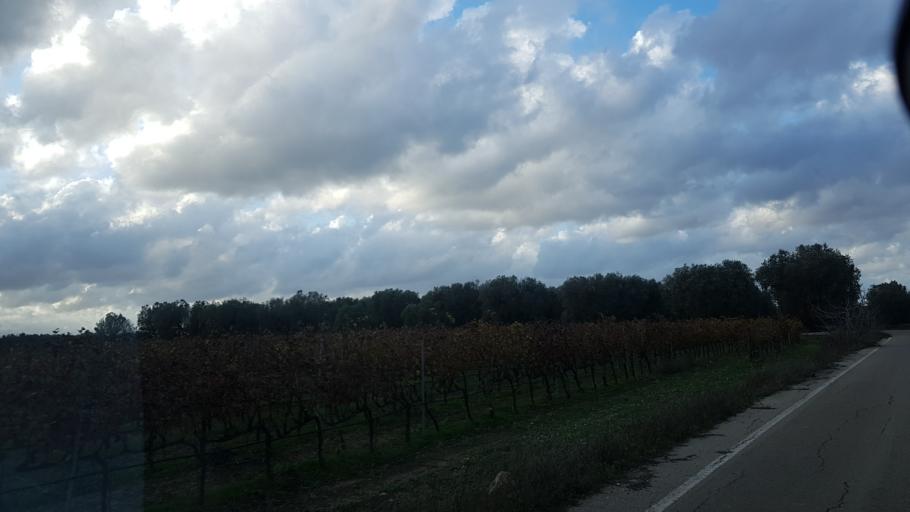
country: IT
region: Apulia
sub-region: Provincia di Brindisi
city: San Pietro Vernotico
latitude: 40.5113
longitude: 18.0191
